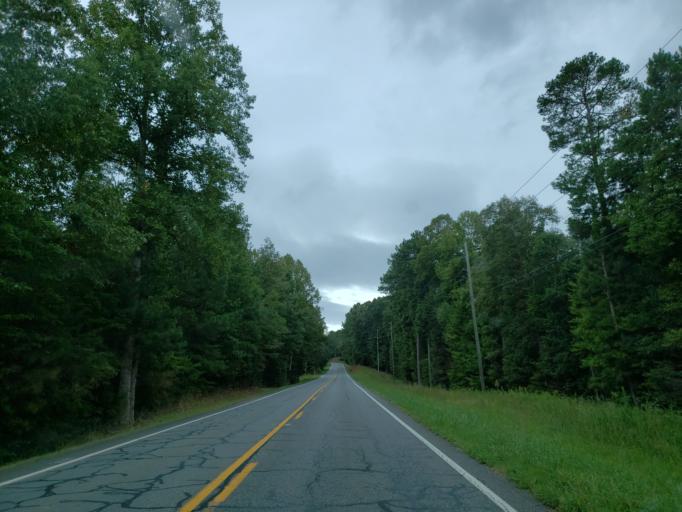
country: US
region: Georgia
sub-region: Gilmer County
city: Ellijay
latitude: 34.6365
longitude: -84.5777
